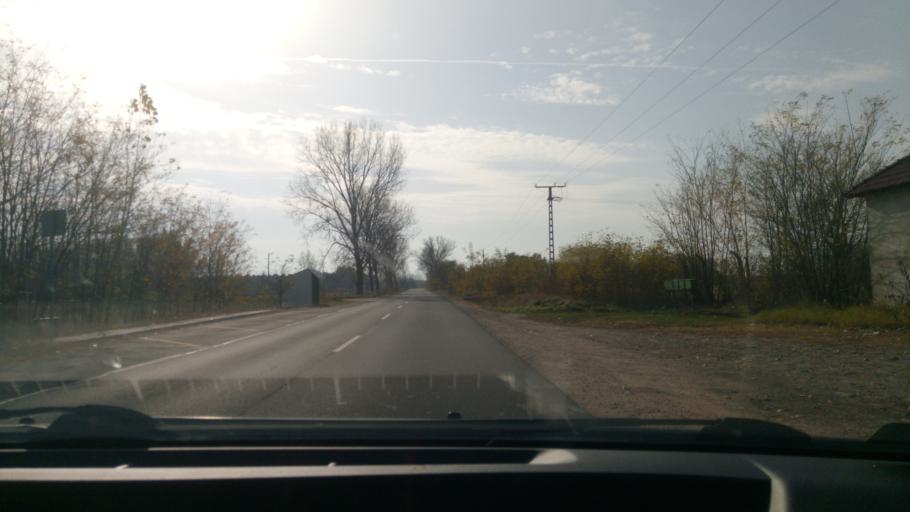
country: HU
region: Bacs-Kiskun
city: Jaszszentlaszlo
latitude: 46.6133
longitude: 19.7950
